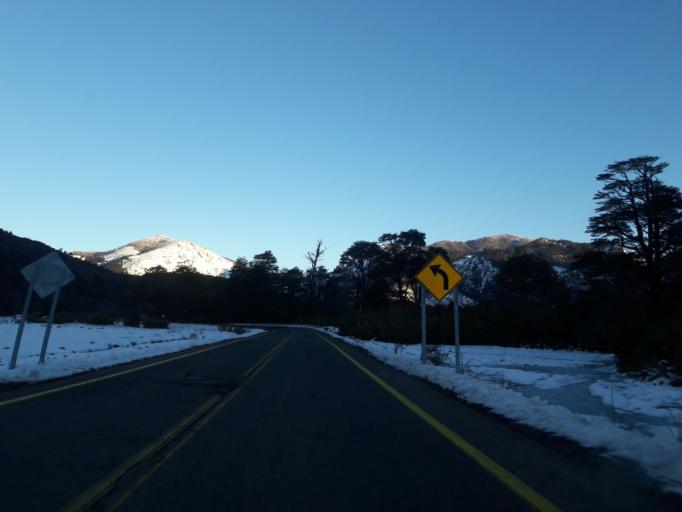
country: CL
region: Araucania
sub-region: Provincia de Cautin
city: Vilcun
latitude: -38.4932
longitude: -71.5222
